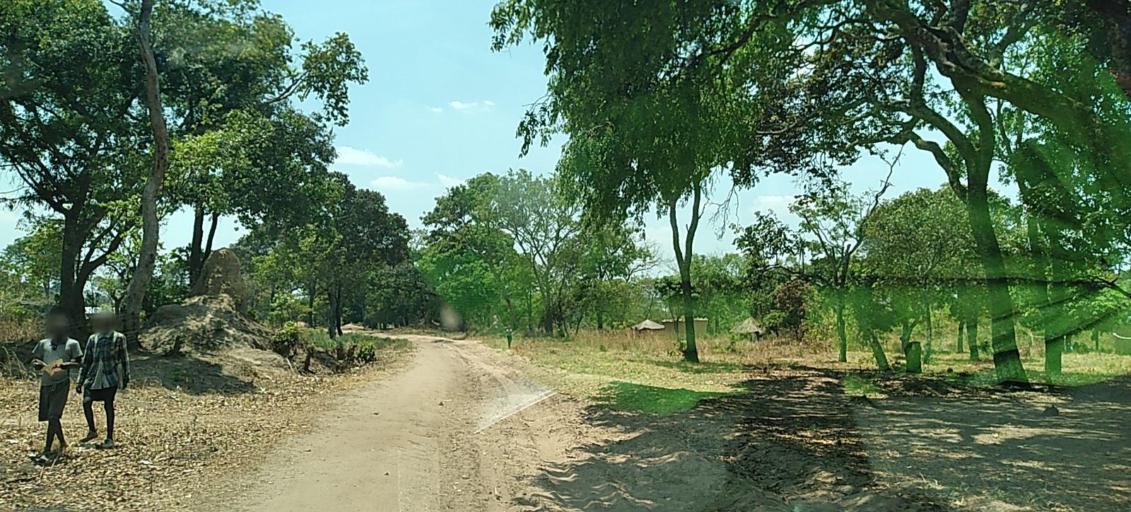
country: CD
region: Katanga
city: Kolwezi
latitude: -11.3746
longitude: 25.2155
